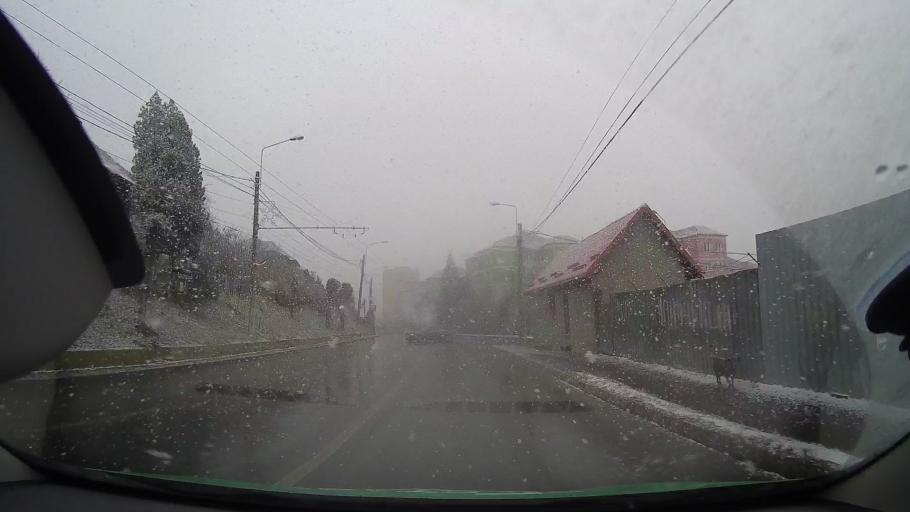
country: RO
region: Sibiu
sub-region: Municipiul Medias
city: Medias
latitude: 46.1713
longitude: 24.3418
